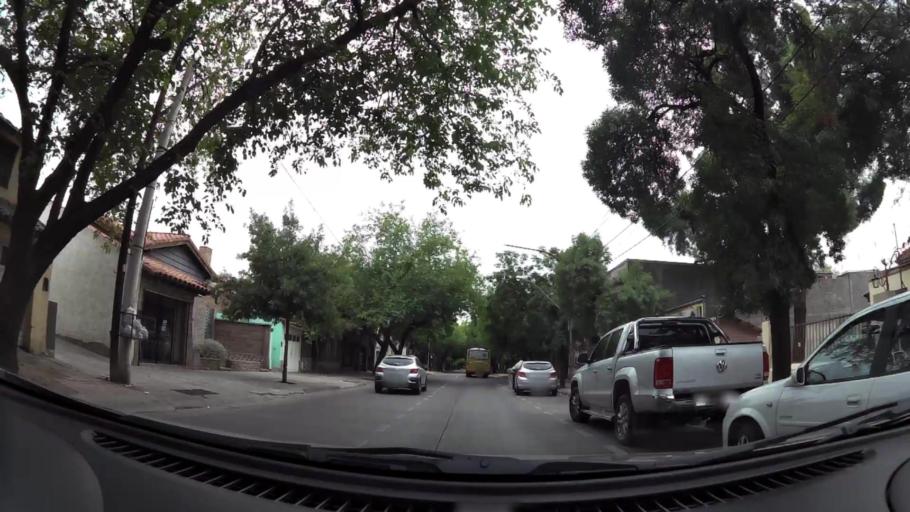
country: AR
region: Mendoza
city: Mendoza
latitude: -32.8987
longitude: -68.8596
